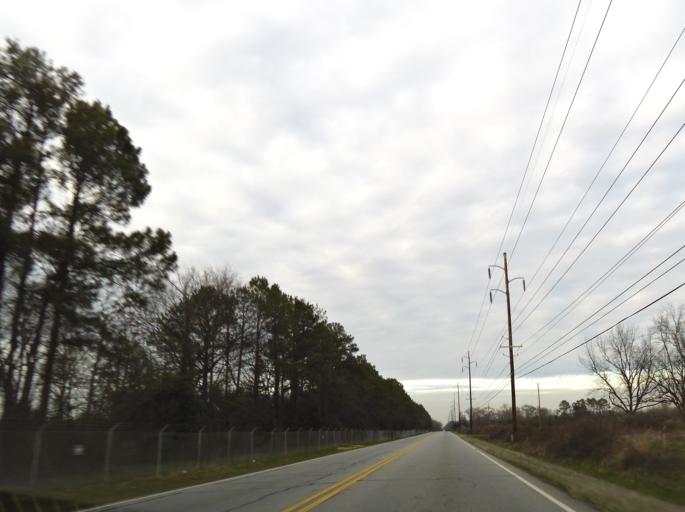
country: US
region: Georgia
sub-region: Houston County
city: Centerville
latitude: 32.6547
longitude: -83.7087
